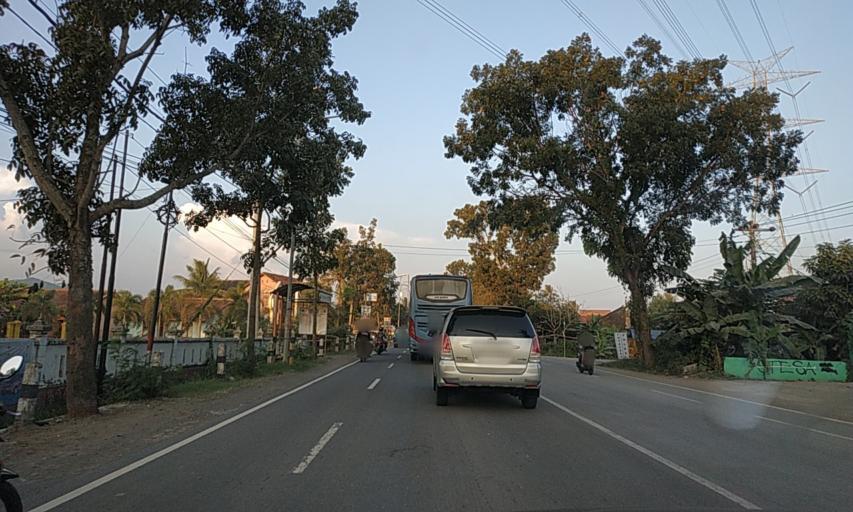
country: ID
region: Daerah Istimewa Yogyakarta
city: Srandakan
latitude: -7.8867
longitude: 110.0573
